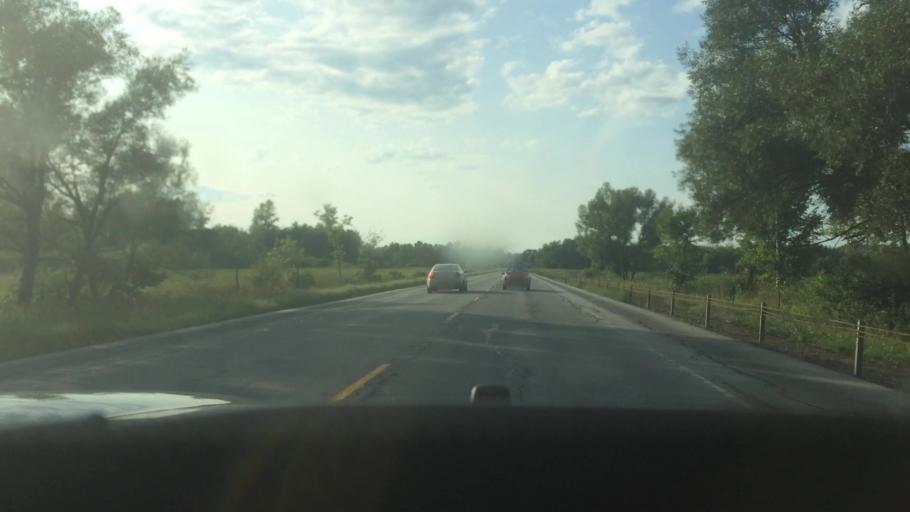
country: US
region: New York
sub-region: St. Lawrence County
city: Canton
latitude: 44.6142
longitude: -75.2177
